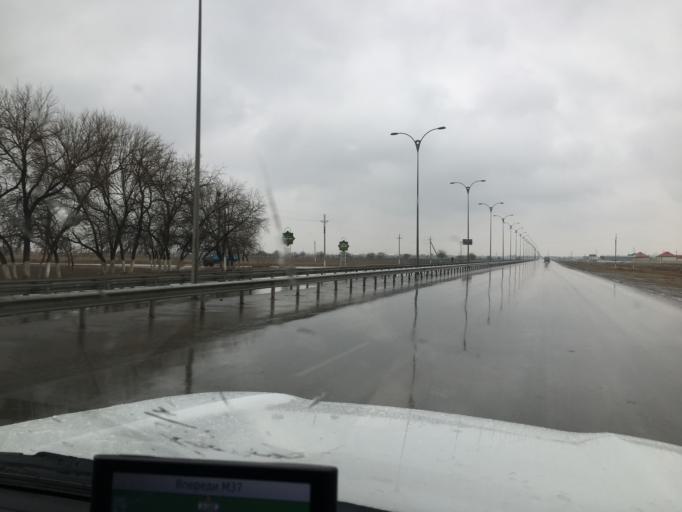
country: TM
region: Mary
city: Mary
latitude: 37.5565
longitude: 61.8551
